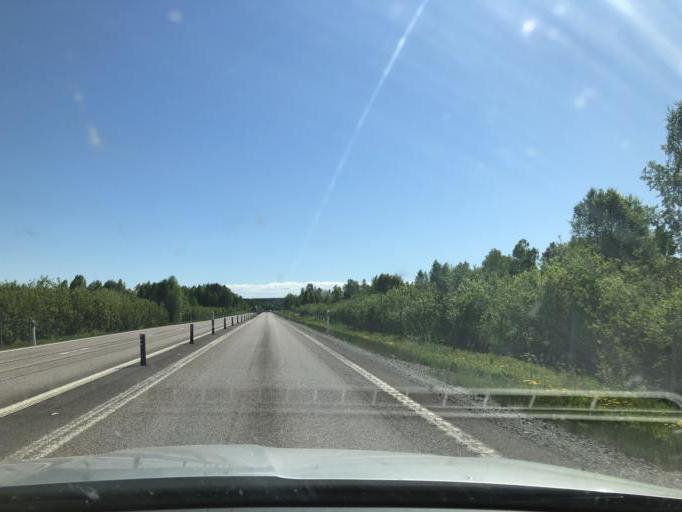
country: SE
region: Norrbotten
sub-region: Kalix Kommun
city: Rolfs
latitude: 65.8920
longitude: 22.9038
